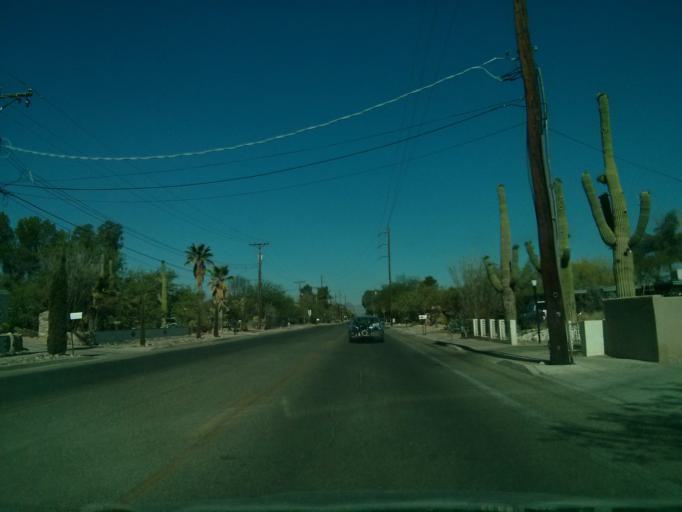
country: US
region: Arizona
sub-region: Pima County
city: Catalina Foothills
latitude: 32.2579
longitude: -110.8937
